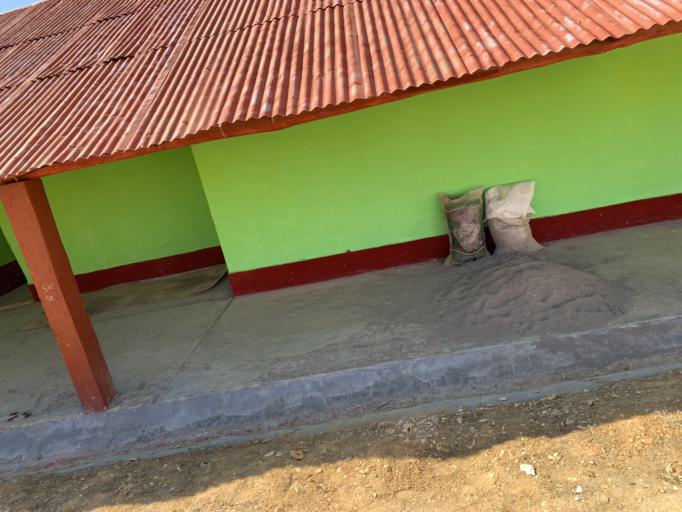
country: PE
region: Huancavelica
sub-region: Provincia de Huancavelica
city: Acobambilla
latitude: -12.6379
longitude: -75.5333
